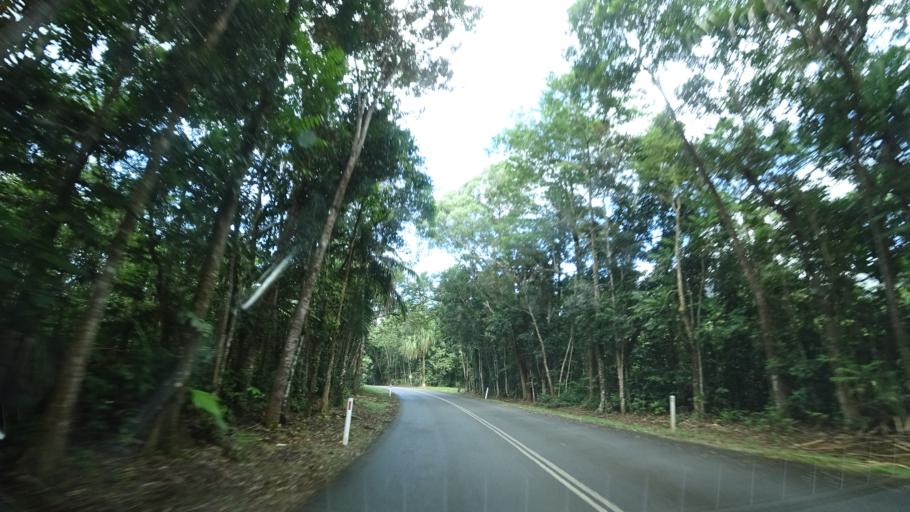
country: AU
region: Queensland
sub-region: Cairns
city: Port Douglas
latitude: -16.1747
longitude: 145.4153
